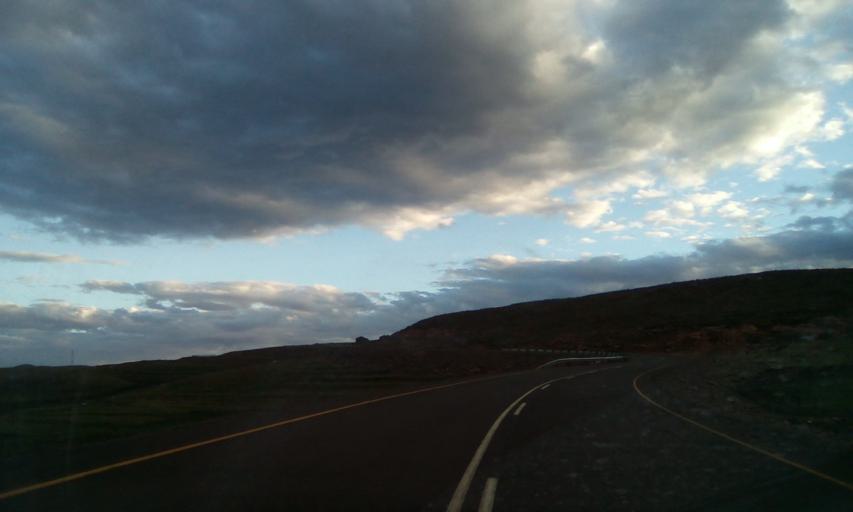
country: LS
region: Maseru
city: Nako
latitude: -29.8127
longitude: 28.0331
